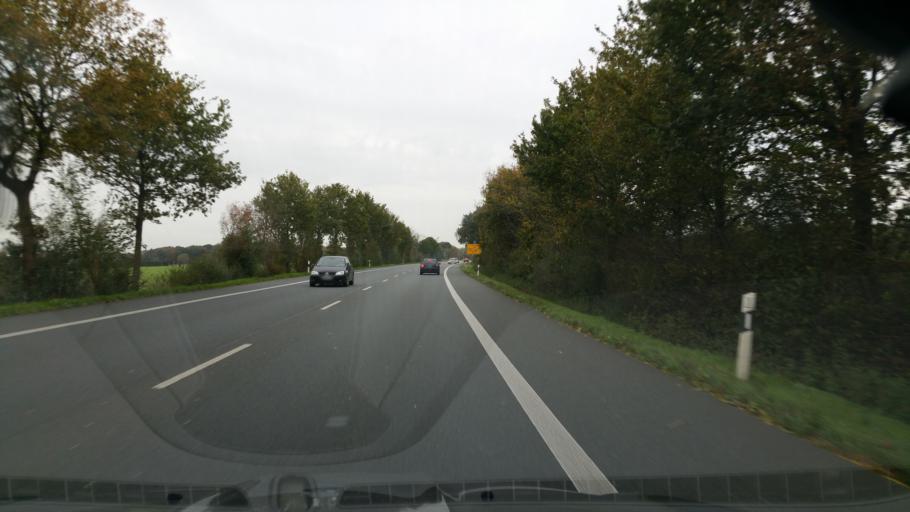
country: DE
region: North Rhine-Westphalia
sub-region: Regierungsbezirk Dusseldorf
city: Hamminkeln
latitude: 51.7636
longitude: 6.5830
